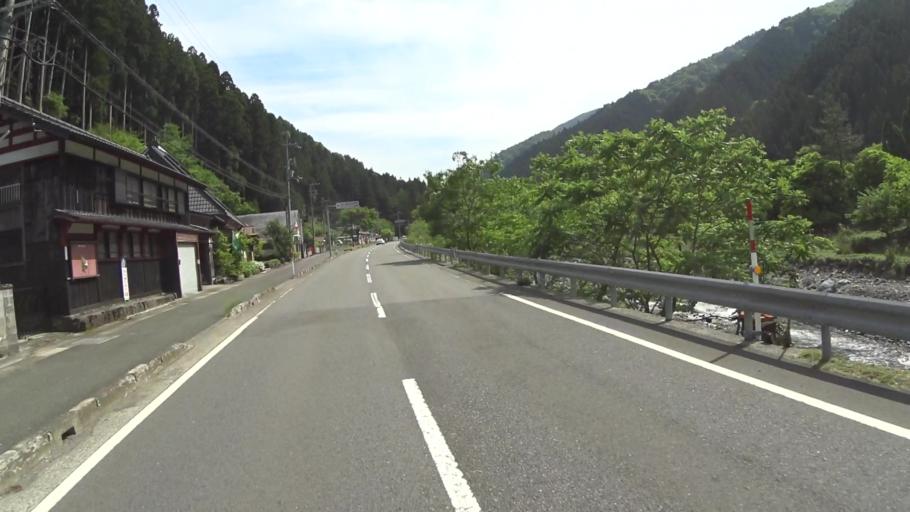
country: JP
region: Shiga Prefecture
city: Kitahama
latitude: 35.2457
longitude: 135.8670
